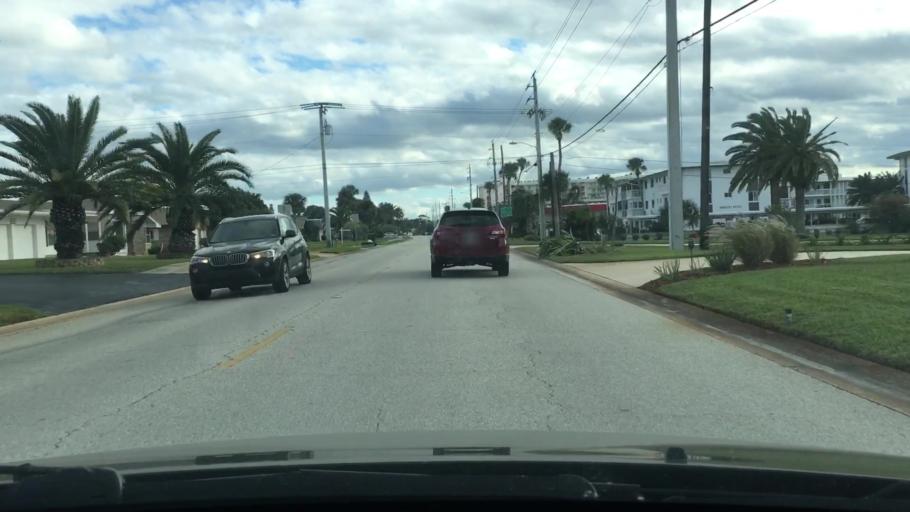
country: US
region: Florida
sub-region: Volusia County
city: Holly Hill
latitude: 29.2660
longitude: -81.0360
